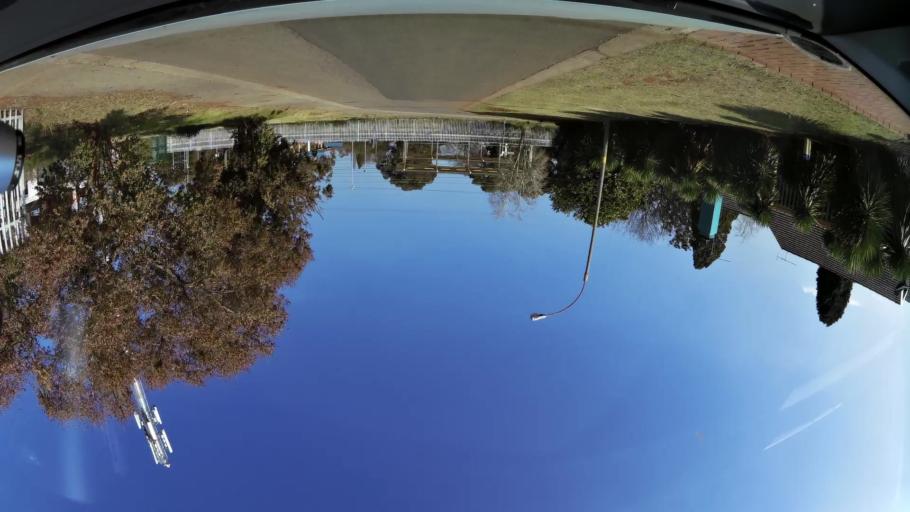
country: ZA
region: Gauteng
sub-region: City of Johannesburg Metropolitan Municipality
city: Modderfontein
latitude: -26.1251
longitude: 28.2246
